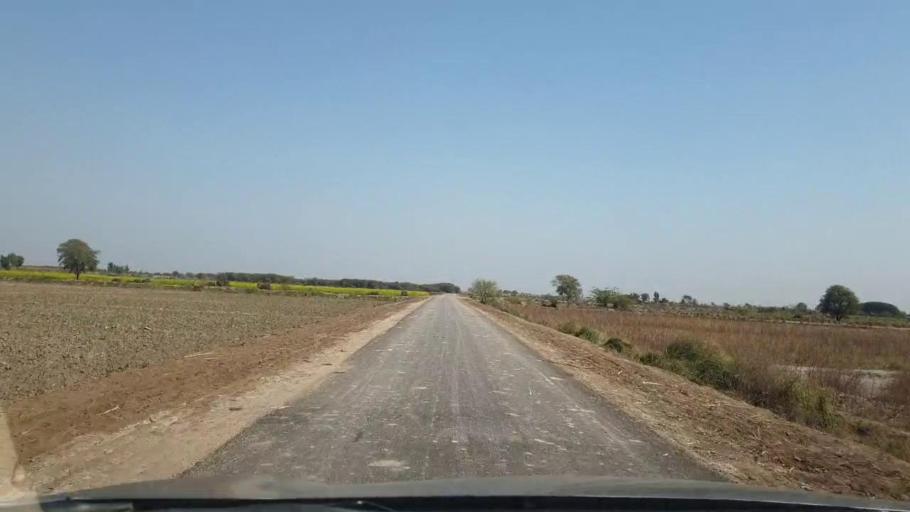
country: PK
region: Sindh
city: Mirpur Khas
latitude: 25.5670
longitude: 68.8866
